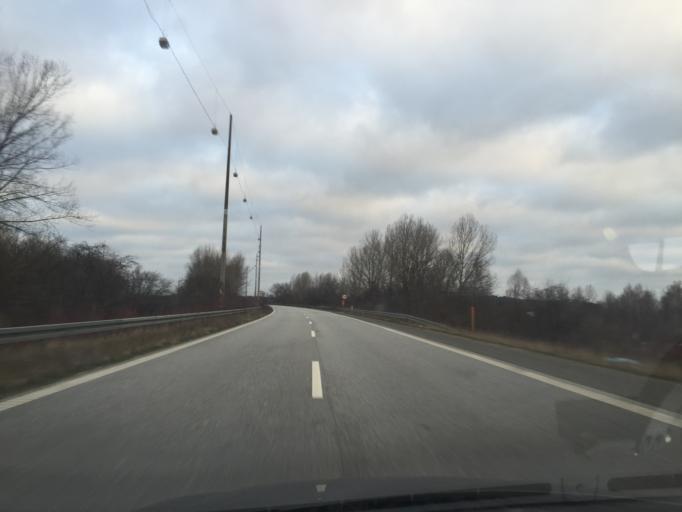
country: DK
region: Capital Region
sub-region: Ishoj Kommune
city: Ishoj
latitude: 55.6387
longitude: 12.3366
